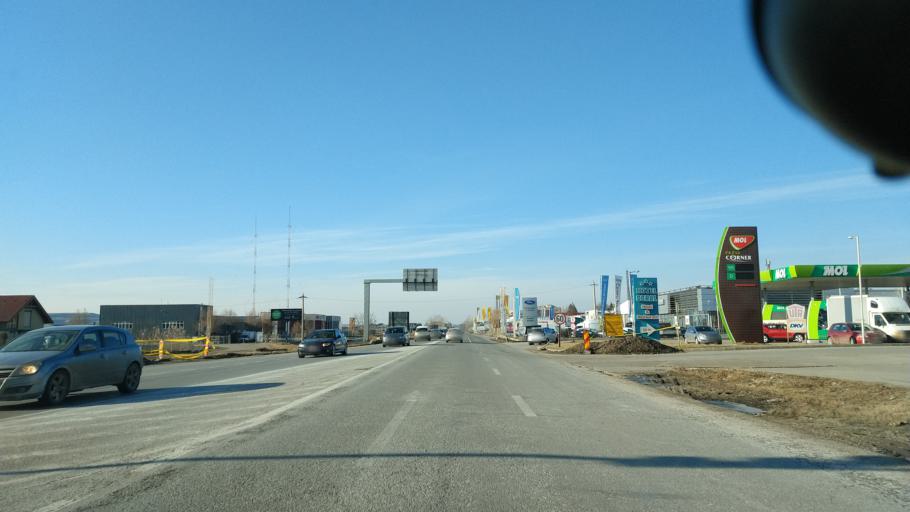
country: RO
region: Iasi
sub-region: Comuna Valea Lupului
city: Valea Lupului
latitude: 47.1818
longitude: 27.4690
